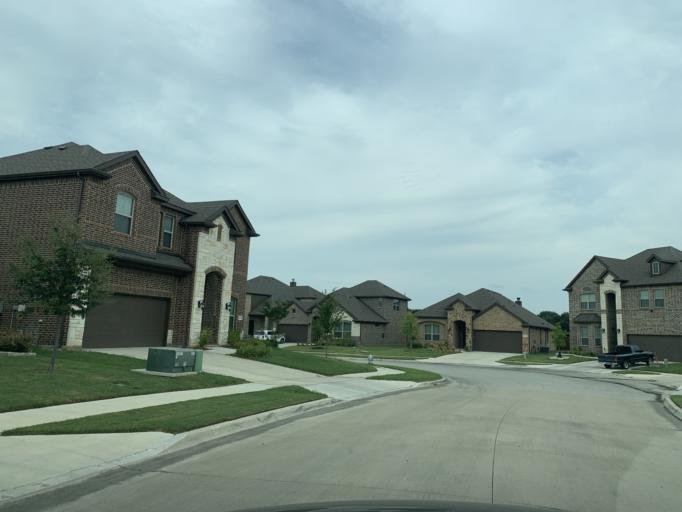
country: US
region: Texas
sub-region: Tarrant County
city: Watauga
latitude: 32.8502
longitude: -97.2916
